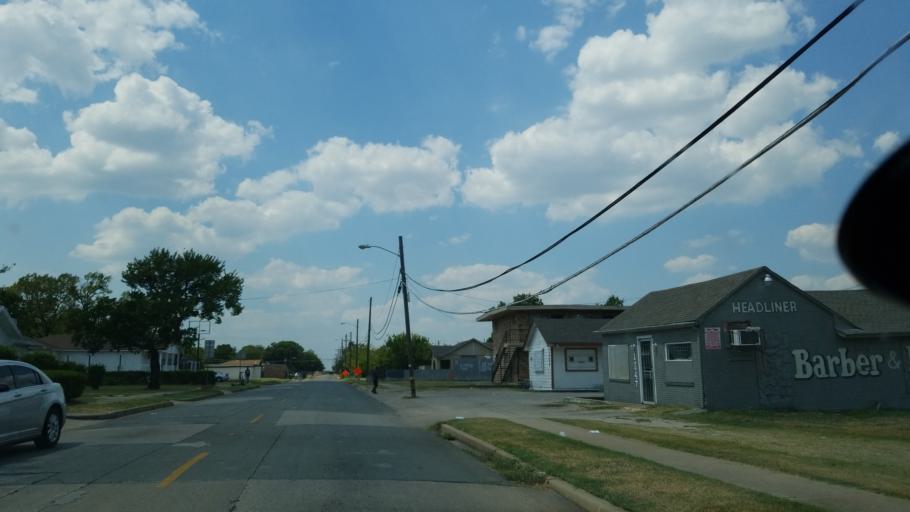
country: US
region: Texas
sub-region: Dallas County
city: Dallas
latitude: 32.7392
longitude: -96.8032
